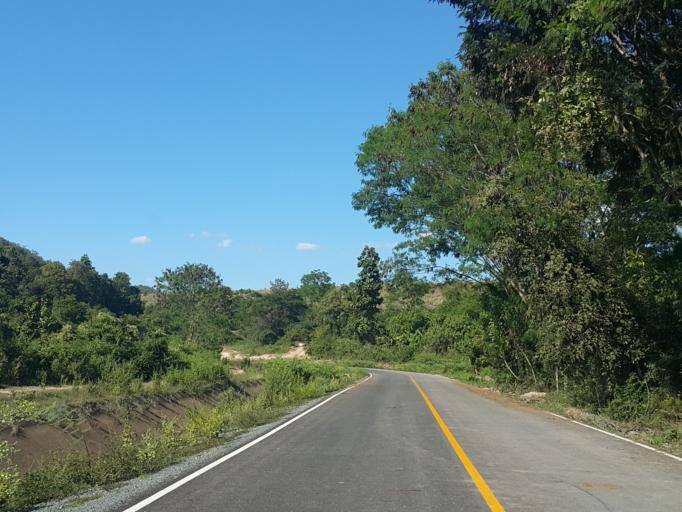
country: TH
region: Chiang Mai
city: San Sai
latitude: 18.9215
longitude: 99.1141
